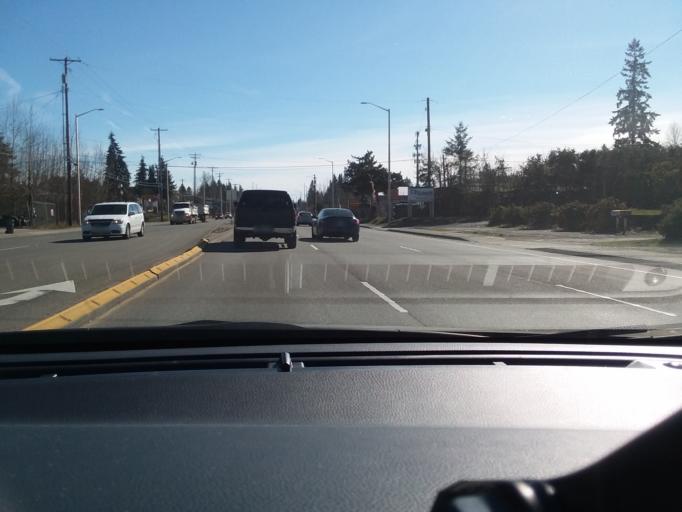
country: US
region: Washington
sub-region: Pierce County
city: Summit
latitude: 47.1300
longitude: -122.3575
